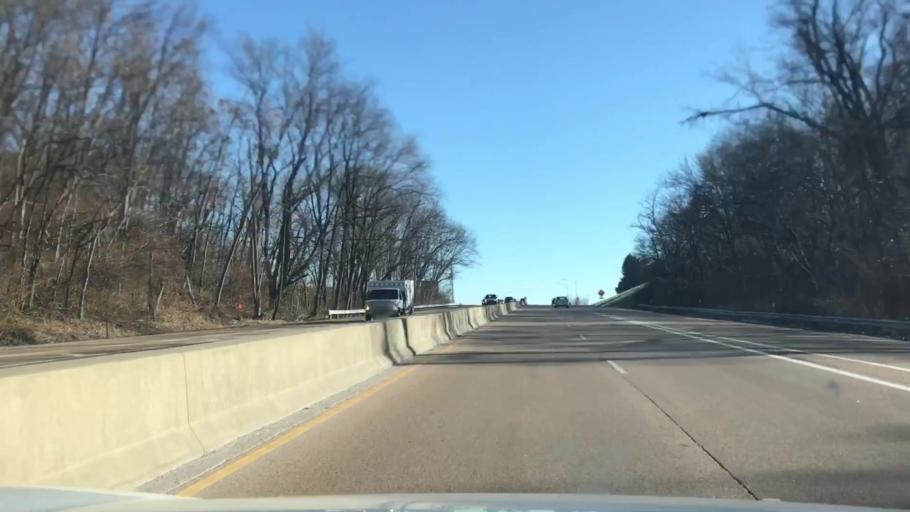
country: US
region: Illinois
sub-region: Saint Clair County
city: Alorton
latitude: 38.5652
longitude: -90.0888
